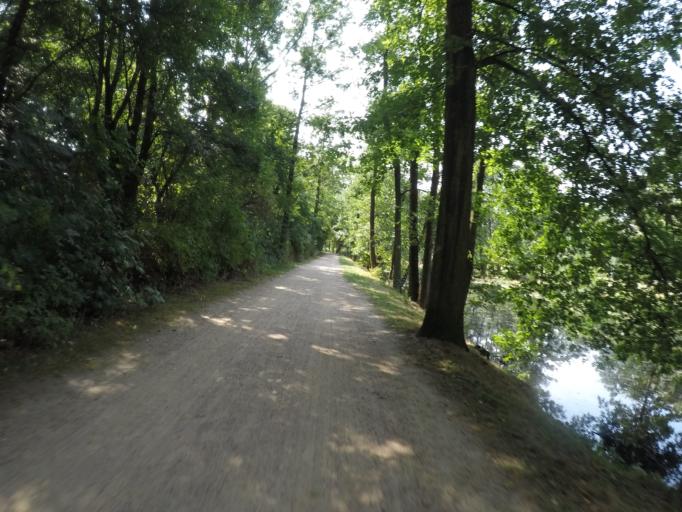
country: DE
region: Hamburg
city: Kleiner Grasbrook
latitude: 53.4984
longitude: 9.9954
